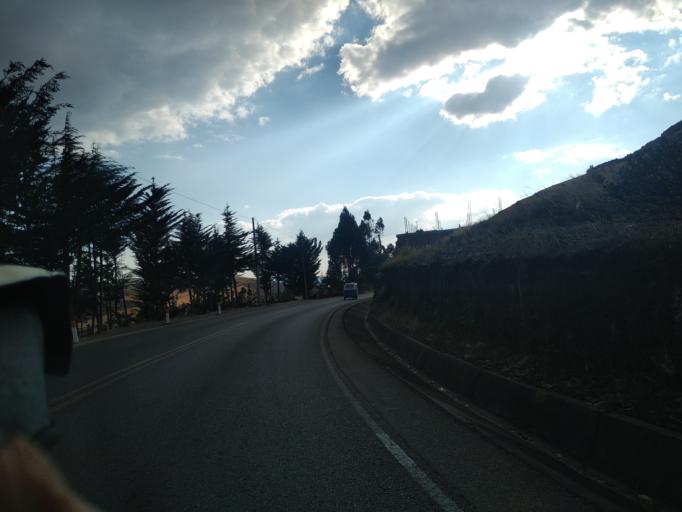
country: PE
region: Cajamarca
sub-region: Provincia de Cajamarca
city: Llacanora
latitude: -7.1543
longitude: -78.4146
